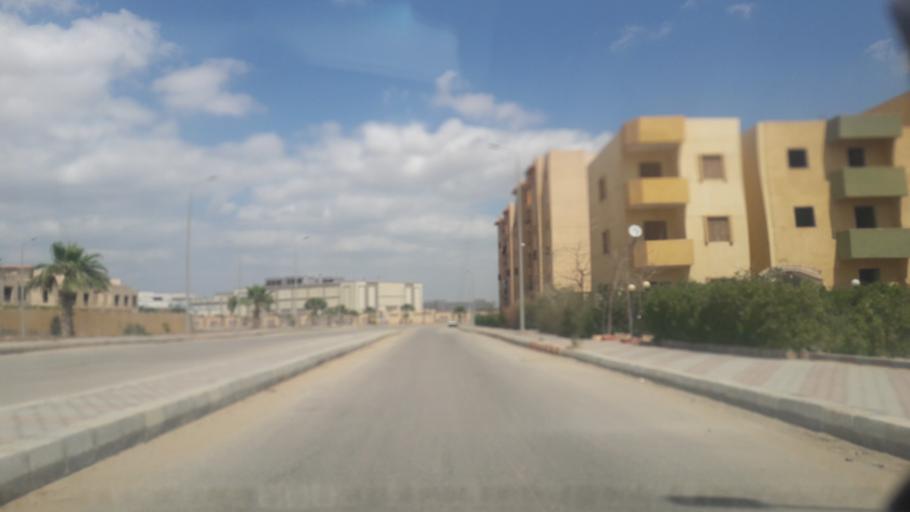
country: EG
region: Al Jizah
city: Madinat Sittah Uktubar
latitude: 29.9355
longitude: 31.0631
